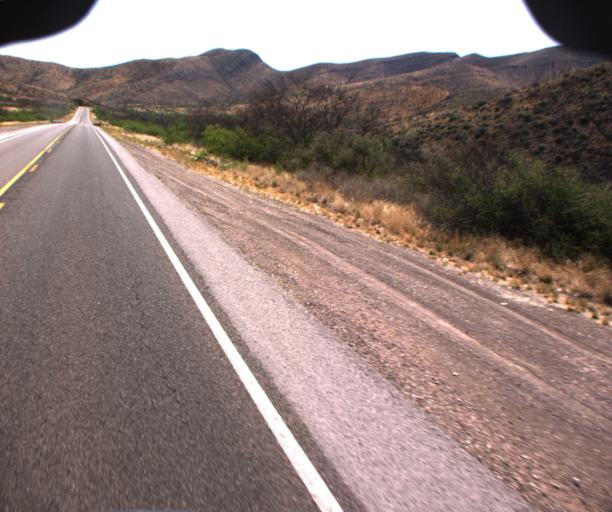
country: US
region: Arizona
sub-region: Cochise County
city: Bisbee
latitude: 31.4317
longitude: -109.8524
